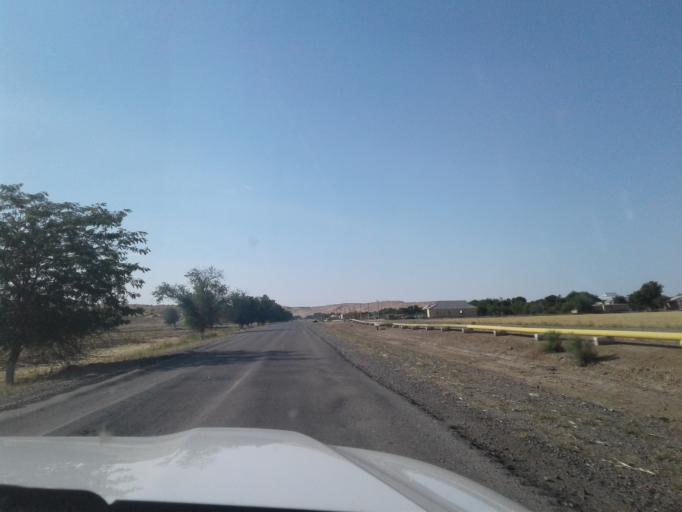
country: TM
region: Mary
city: Yoloeten
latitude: 36.7001
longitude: 62.4581
